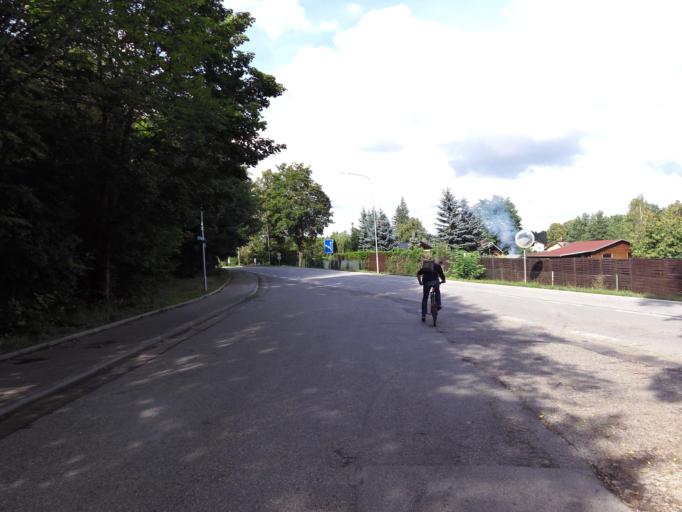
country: CZ
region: Jihocesky
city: Suchdol nad Luznici
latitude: 48.8936
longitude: 14.8808
